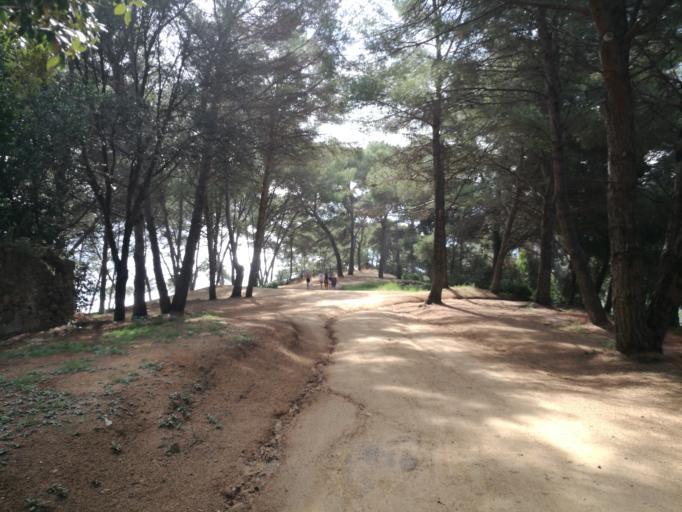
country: ES
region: Catalonia
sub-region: Provincia de Girona
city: Blanes
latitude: 41.6869
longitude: 2.8150
